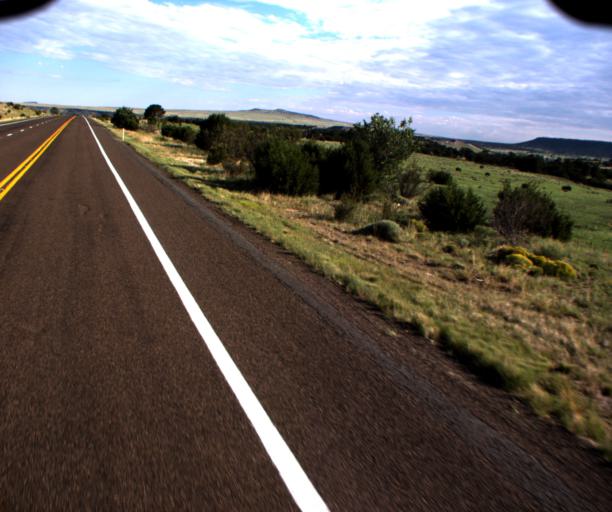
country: US
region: Arizona
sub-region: Apache County
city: Eagar
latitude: 34.0922
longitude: -109.2430
